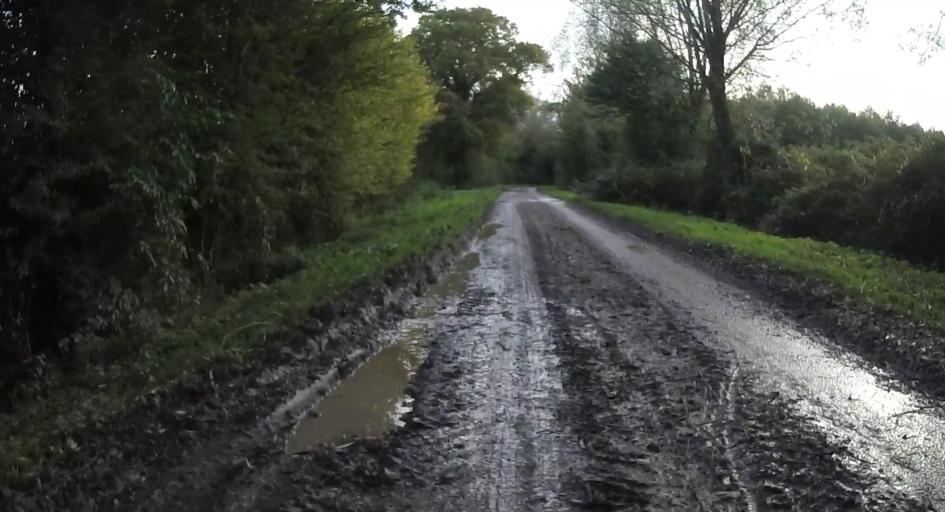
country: GB
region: England
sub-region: Wokingham
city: Swallowfield
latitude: 51.3751
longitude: -0.9601
